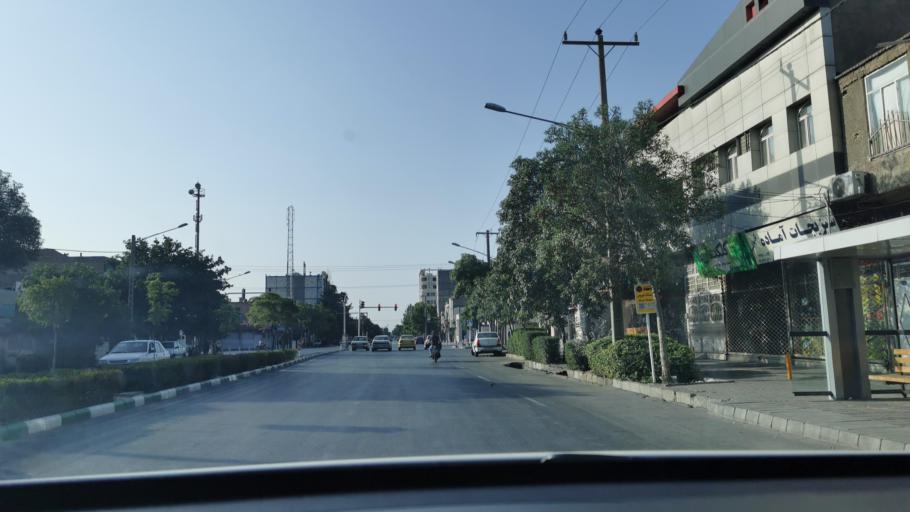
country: IR
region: Razavi Khorasan
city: Mashhad
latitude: 36.3067
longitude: 59.6438
